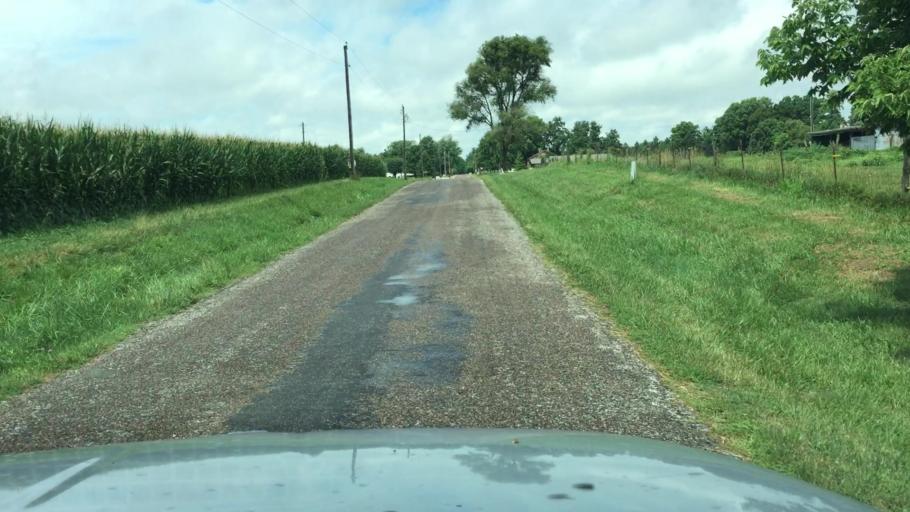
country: US
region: Illinois
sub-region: Hancock County
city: Nauvoo
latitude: 40.5427
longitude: -91.3628
